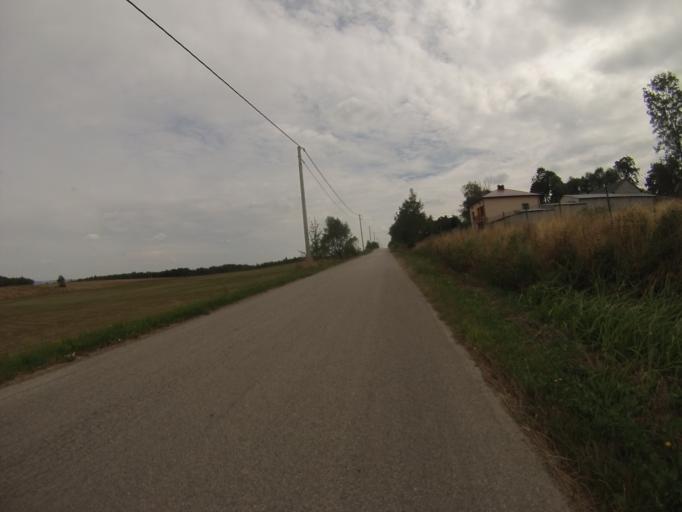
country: PL
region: Swietokrzyskie
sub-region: Powiat kielecki
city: Lagow
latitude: 50.7594
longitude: 21.0904
